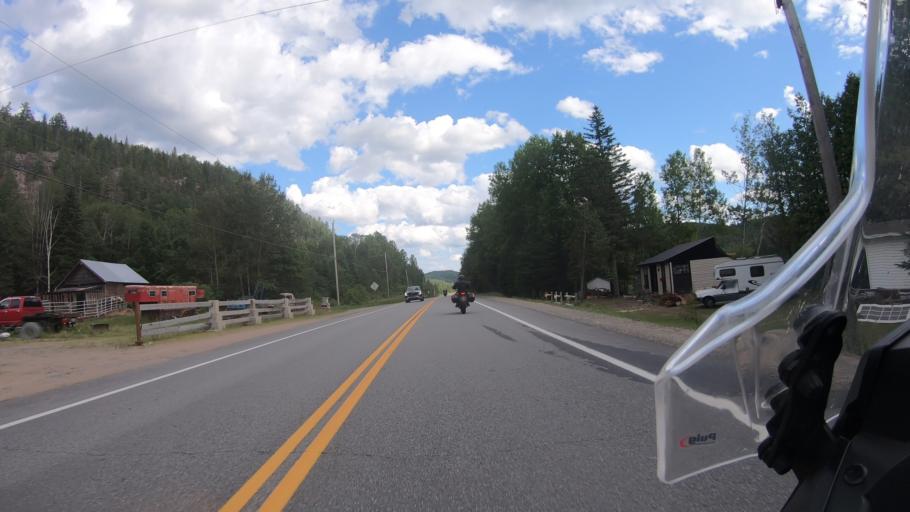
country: CA
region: Quebec
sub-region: Mauricie
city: Saint-Tite
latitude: 46.9925
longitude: -72.9151
